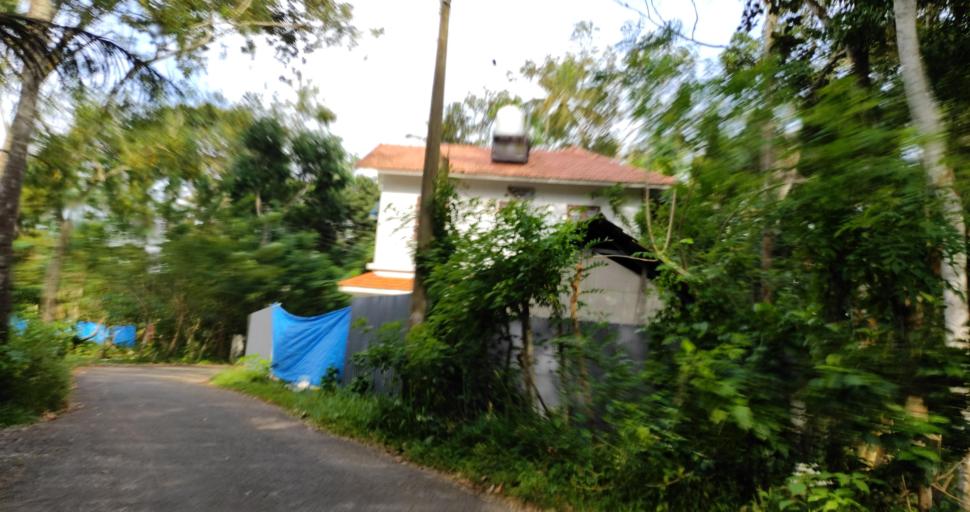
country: IN
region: Kerala
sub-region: Alappuzha
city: Shertallai
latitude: 9.6150
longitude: 76.3438
